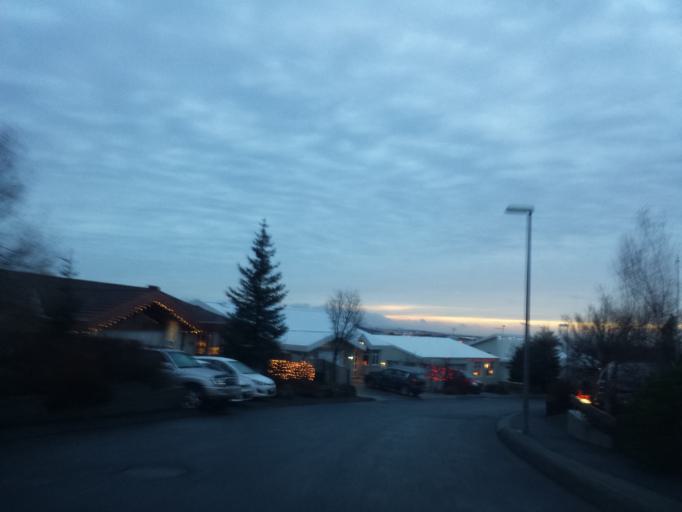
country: IS
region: Capital Region
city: Mosfellsbaer
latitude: 64.1359
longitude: -21.7732
